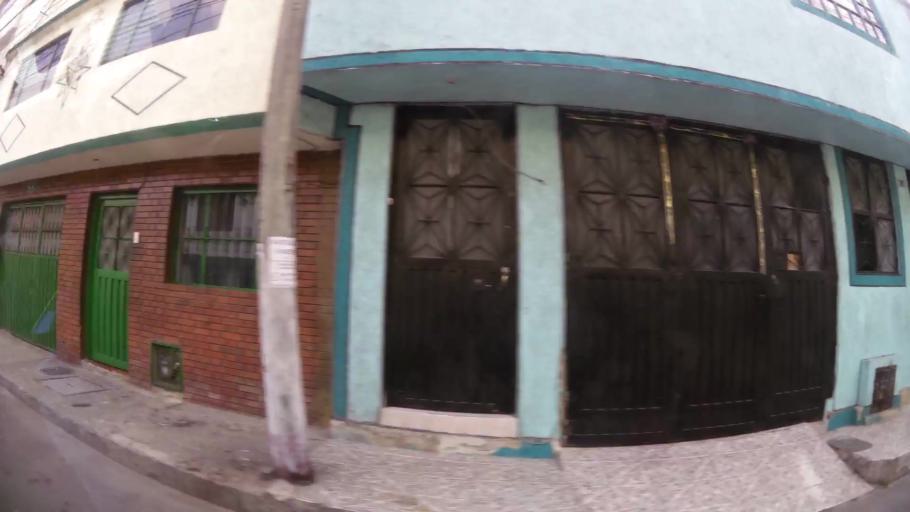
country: CO
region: Bogota D.C.
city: Bogota
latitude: 4.5926
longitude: -74.1167
